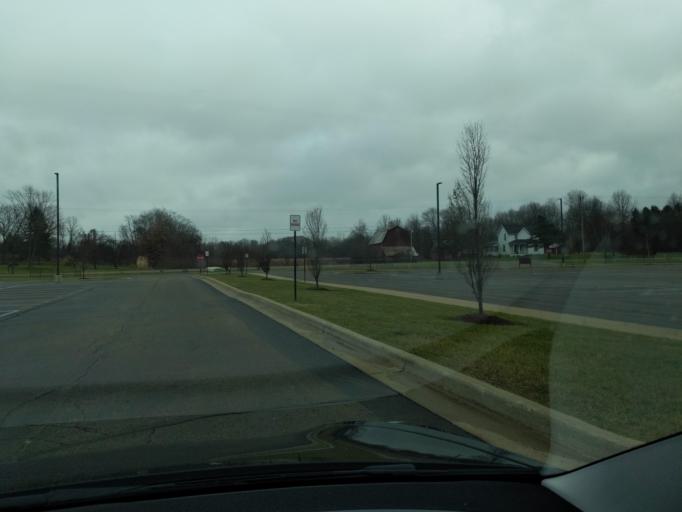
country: US
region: Michigan
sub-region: Jackson County
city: Spring Arbor
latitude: 42.2450
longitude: -84.5388
